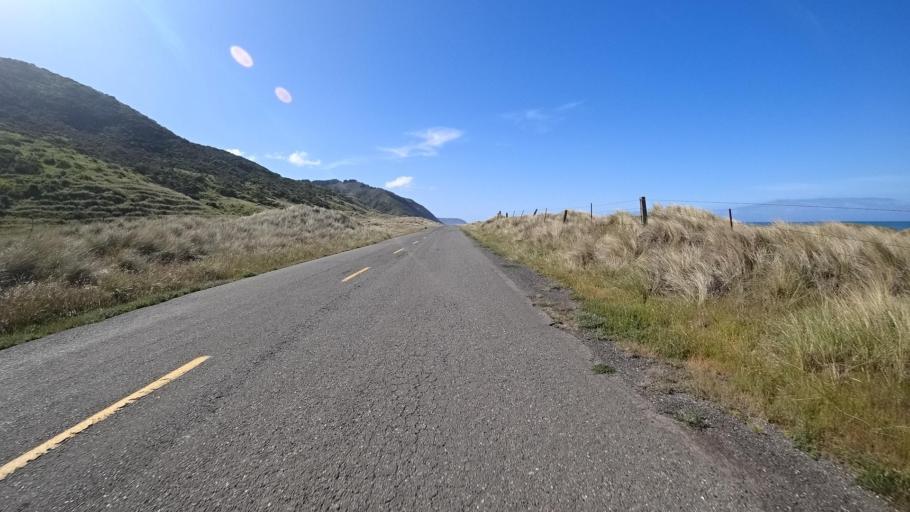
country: US
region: California
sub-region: Humboldt County
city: Ferndale
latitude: 40.3595
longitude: -124.3616
